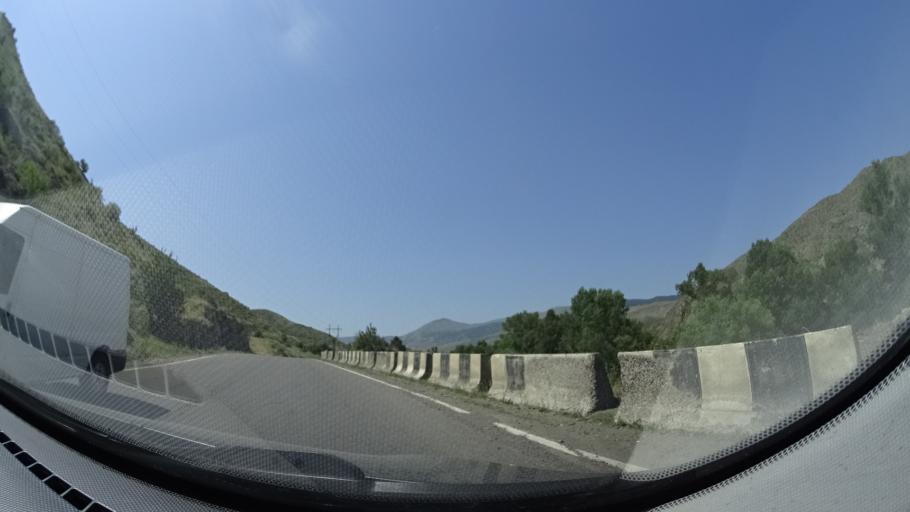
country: GE
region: Samtskhe-Javakheti
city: Aspindza
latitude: 41.5559
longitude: 43.2692
